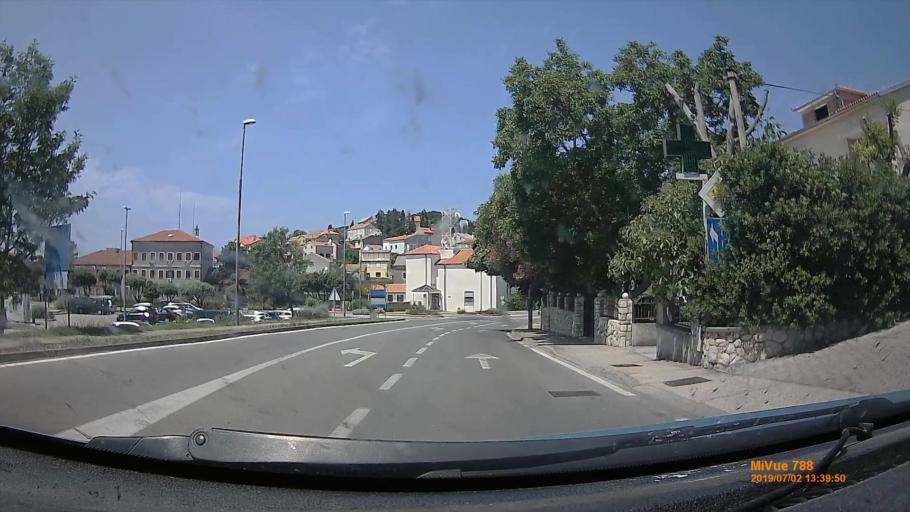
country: HR
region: Primorsko-Goranska
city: Mali Losinj
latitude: 44.5288
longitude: 14.4769
